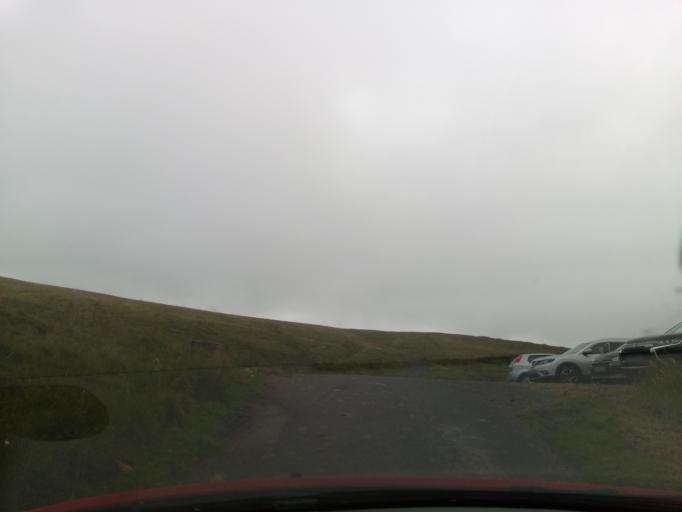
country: GB
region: England
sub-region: Northumberland
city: Rochester
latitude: 55.3702
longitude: -2.3262
